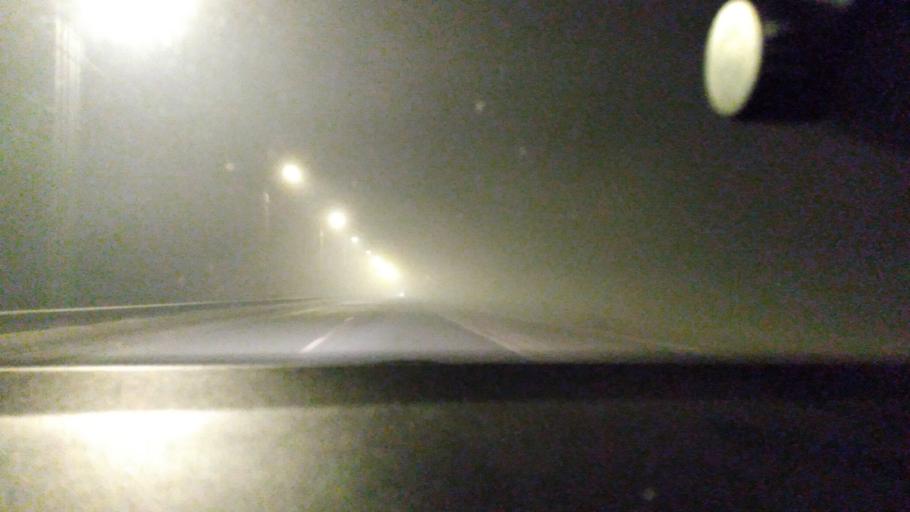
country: RU
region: Moskovskaya
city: Yegor'yevsk
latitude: 55.4001
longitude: 39.0608
